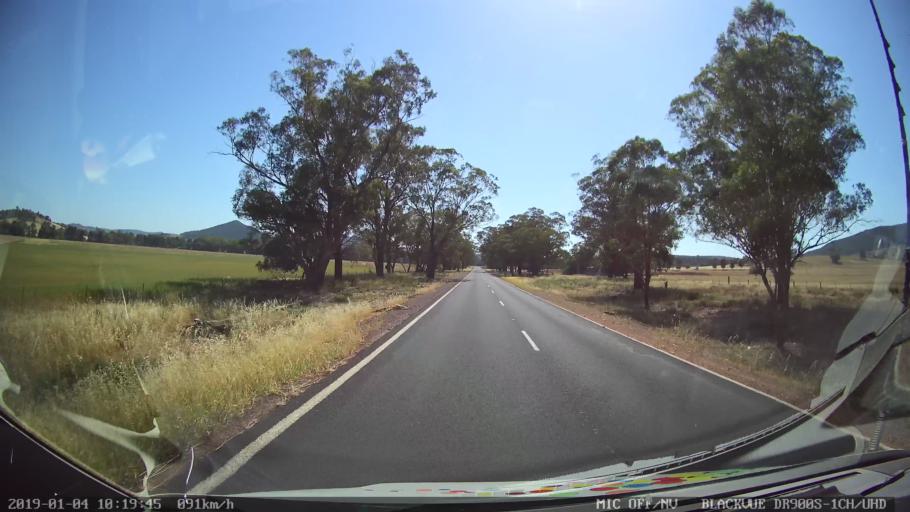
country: AU
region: New South Wales
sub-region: Cabonne
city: Canowindra
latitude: -33.3752
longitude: 148.4853
